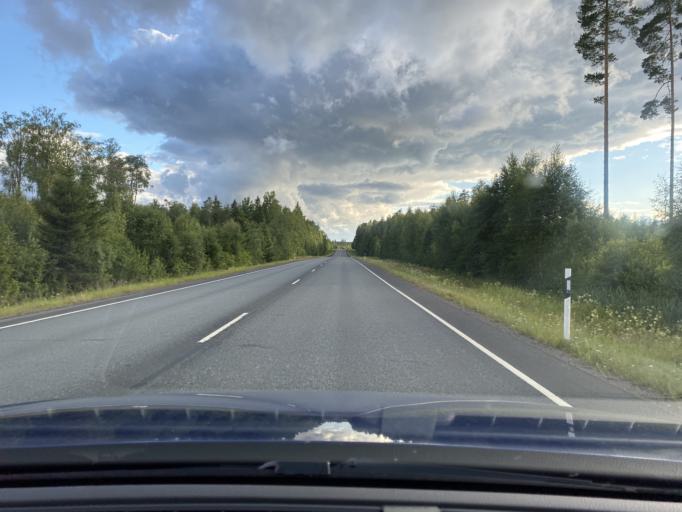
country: FI
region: Haeme
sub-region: Haemeenlinna
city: Renko
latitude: 60.8560
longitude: 24.1671
